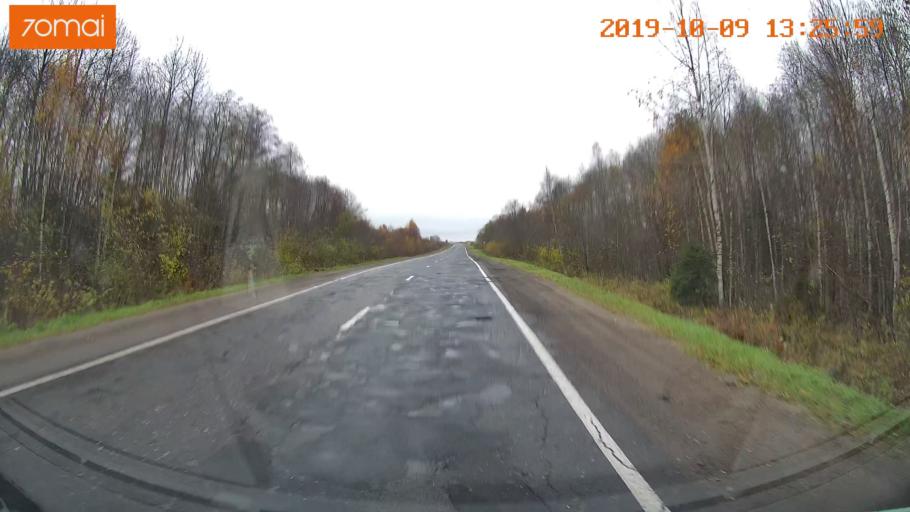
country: RU
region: Jaroslavl
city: Lyubim
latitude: 58.3242
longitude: 40.9188
